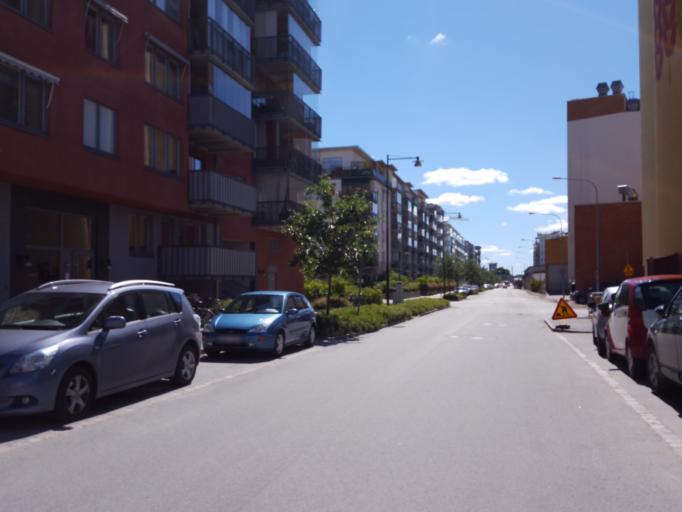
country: SE
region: Uppsala
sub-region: Uppsala Kommun
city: Uppsala
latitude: 59.8511
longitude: 17.6499
